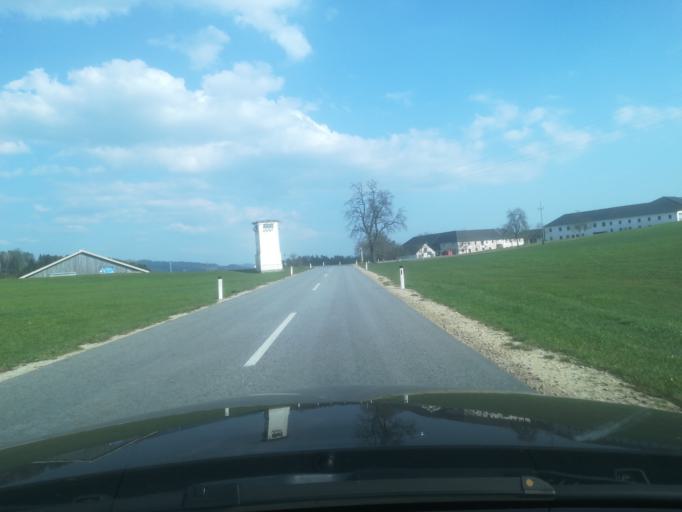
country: AT
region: Upper Austria
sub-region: Politischer Bezirk Perg
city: Perg
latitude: 48.3693
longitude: 14.6456
